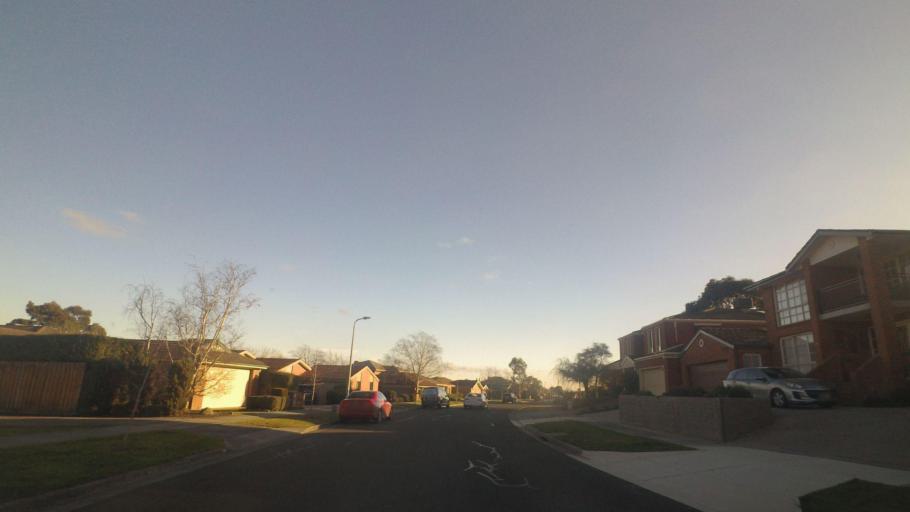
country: AU
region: Victoria
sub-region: Knox
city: Rowville
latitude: -37.9234
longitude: 145.2622
